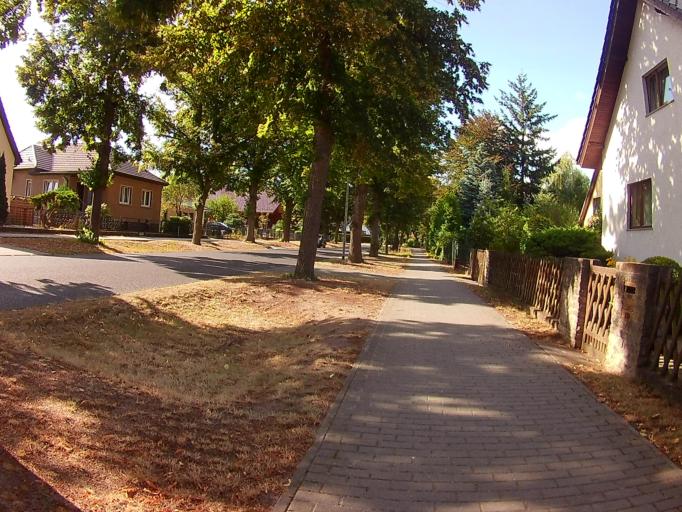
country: DE
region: Brandenburg
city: Schulzendorf
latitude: 52.3774
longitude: 13.5986
